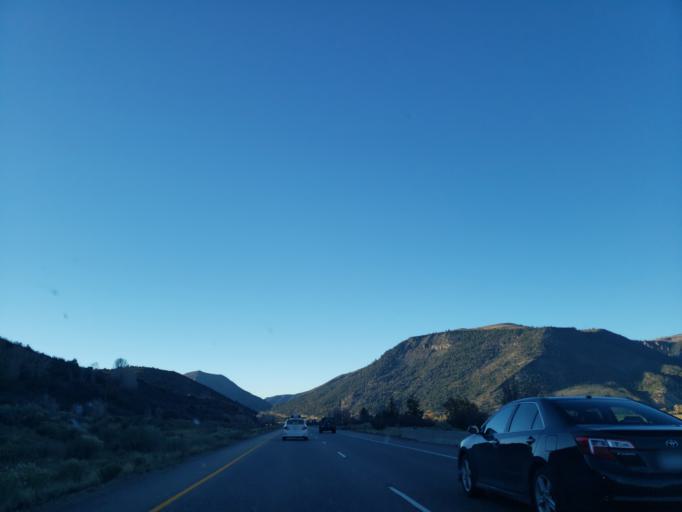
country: US
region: Colorado
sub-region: Pitkin County
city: Snowmass Village
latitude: 39.2781
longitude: -106.8961
